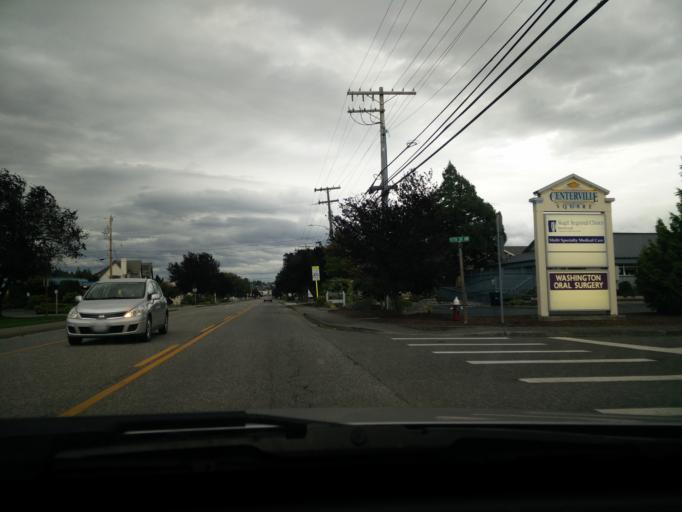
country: US
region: Washington
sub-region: Snohomish County
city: Stanwood
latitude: 48.2421
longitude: -122.3646
